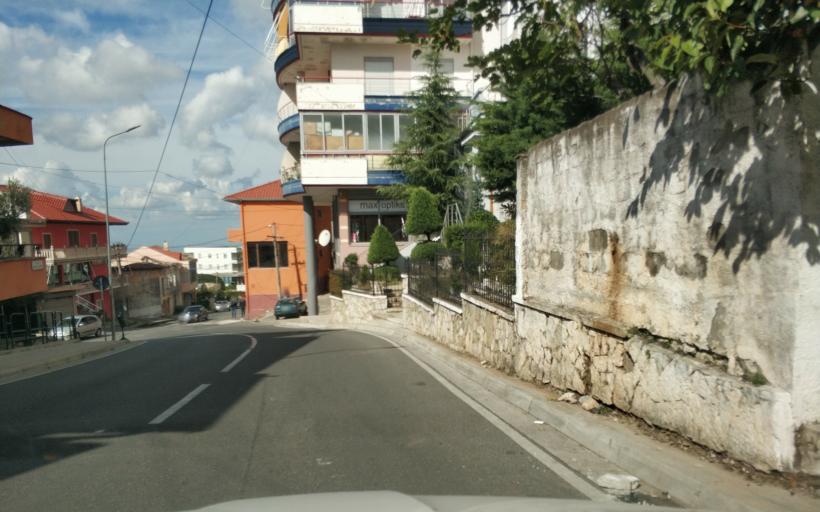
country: AL
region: Durres
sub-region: Rrethi i Krujes
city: Kruje
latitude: 41.5138
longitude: 19.7901
